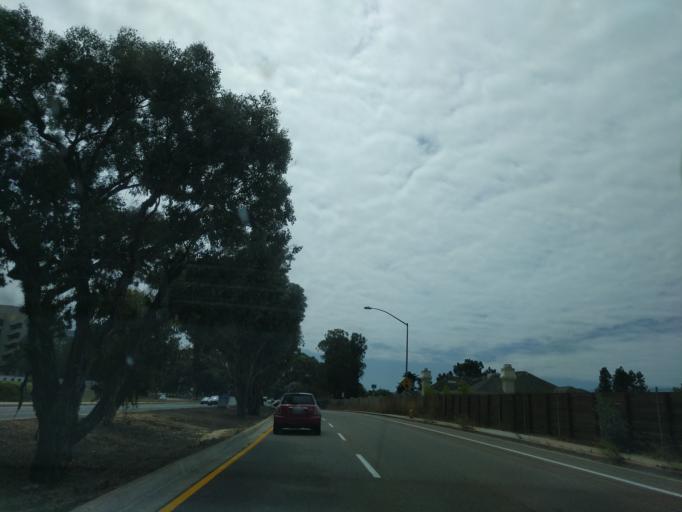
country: US
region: California
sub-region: San Diego County
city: La Jolla
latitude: 32.8782
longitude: -117.2440
